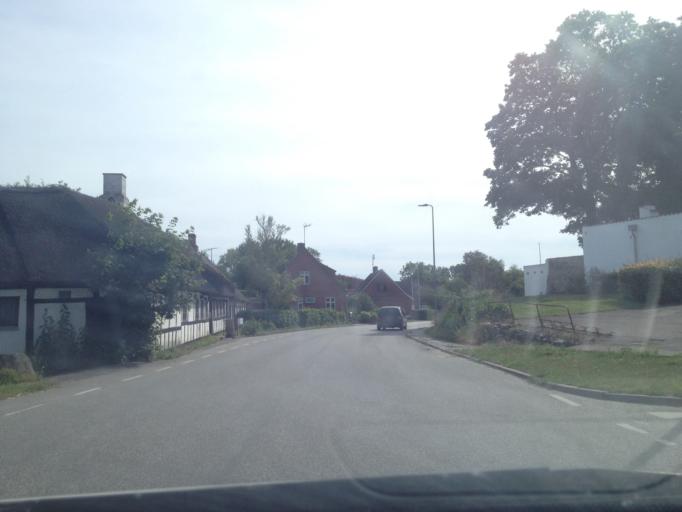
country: DK
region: Central Jutland
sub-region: Samso Kommune
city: Tranebjerg
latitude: 55.8007
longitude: 10.5582
